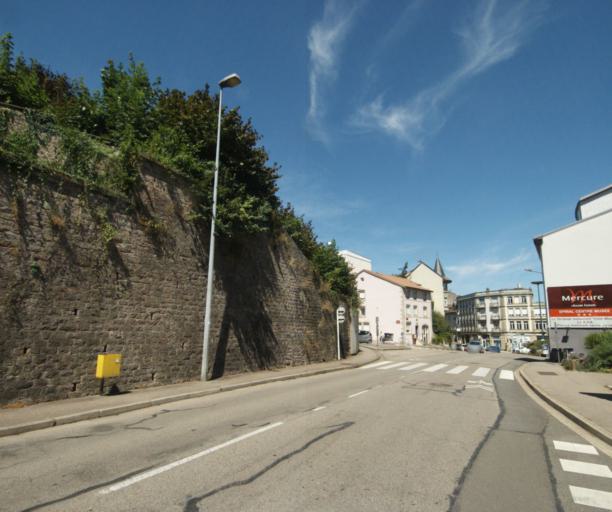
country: FR
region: Lorraine
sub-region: Departement des Vosges
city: Chantraine
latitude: 48.1725
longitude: 6.4451
